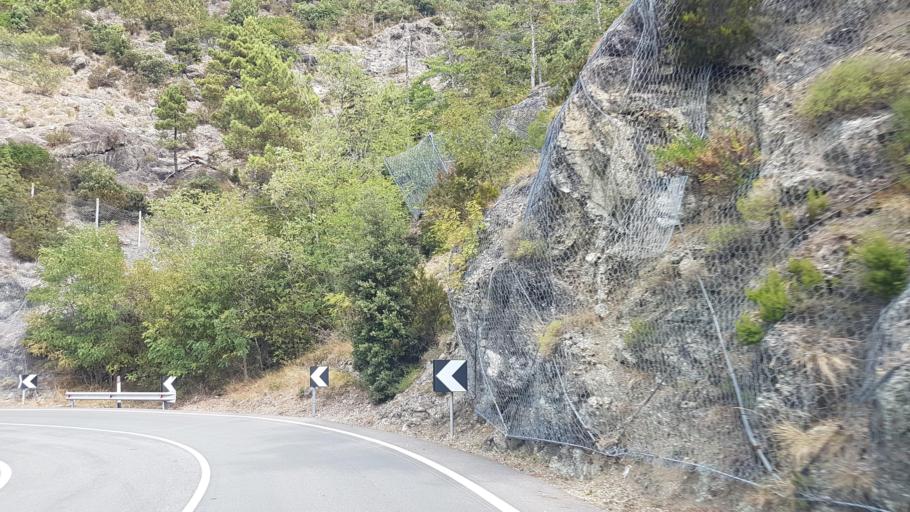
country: IT
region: Liguria
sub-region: Provincia di La Spezia
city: Framura
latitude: 44.2506
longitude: 9.5680
